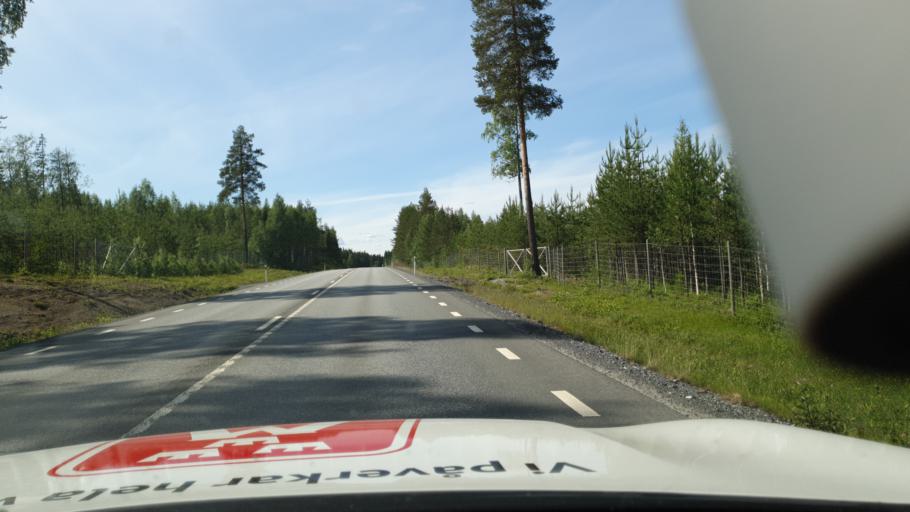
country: SE
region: Vaesterbotten
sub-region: Skelleftea Kommun
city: Forsbacka
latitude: 64.8163
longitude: 20.6197
